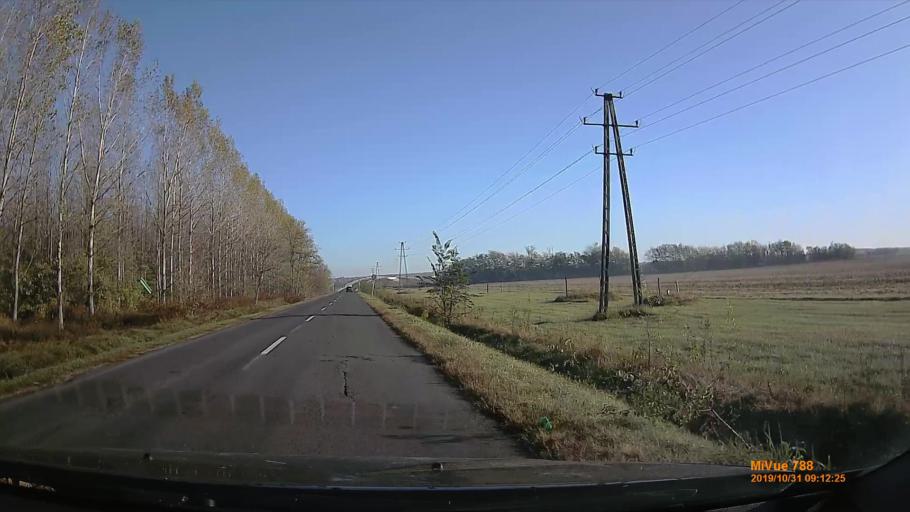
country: HU
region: Pest
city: Peteri
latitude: 47.3739
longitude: 19.3946
